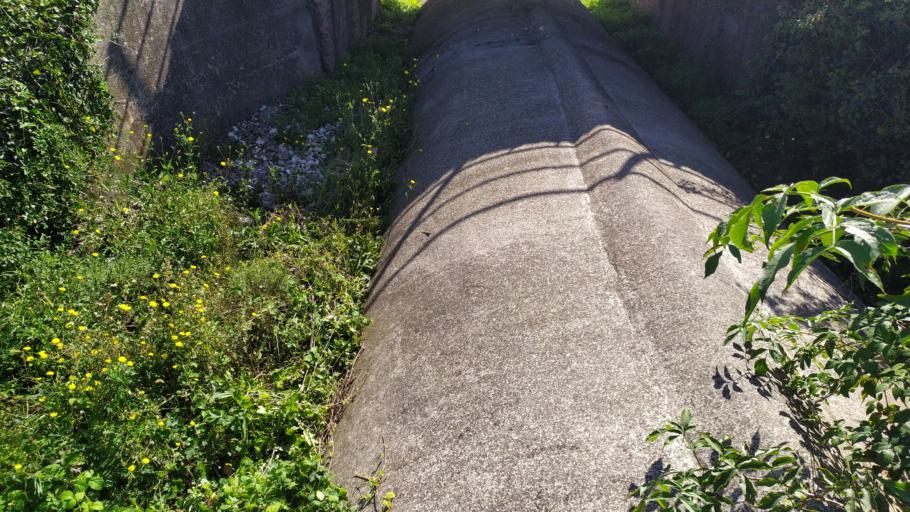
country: IT
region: Friuli Venezia Giulia
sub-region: Provincia di Pordenone
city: Caneva
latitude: 45.9385
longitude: 12.4595
